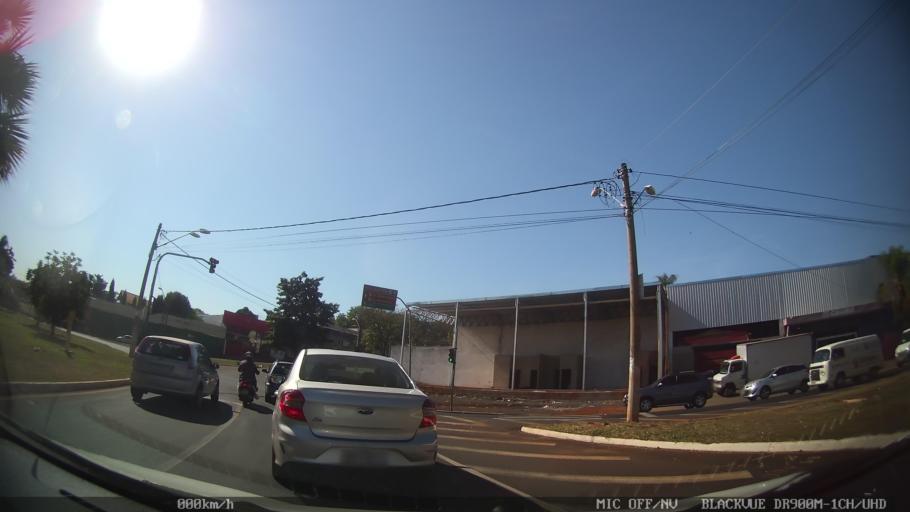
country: BR
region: Sao Paulo
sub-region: Ribeirao Preto
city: Ribeirao Preto
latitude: -21.1955
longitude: -47.8224
